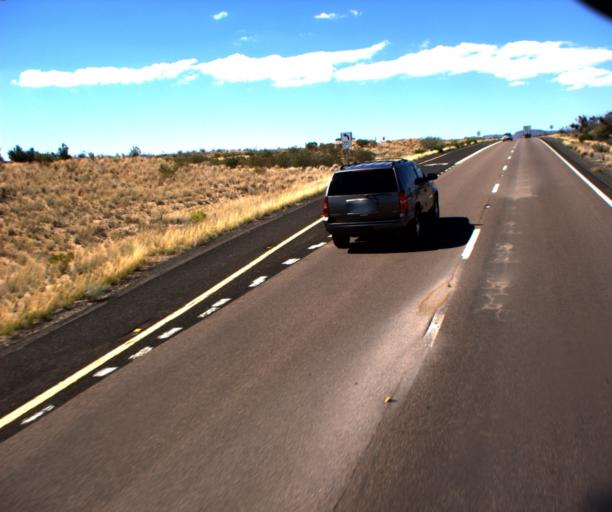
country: US
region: Arizona
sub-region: Mohave County
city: Kingman
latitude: 35.0660
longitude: -113.6650
